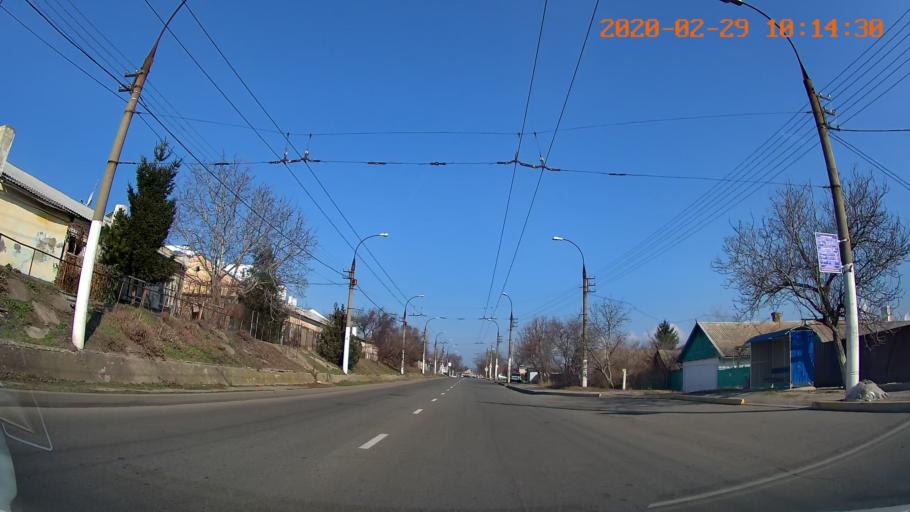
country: MD
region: Telenesti
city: Tiraspolul Nou
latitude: 46.8474
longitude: 29.6435
